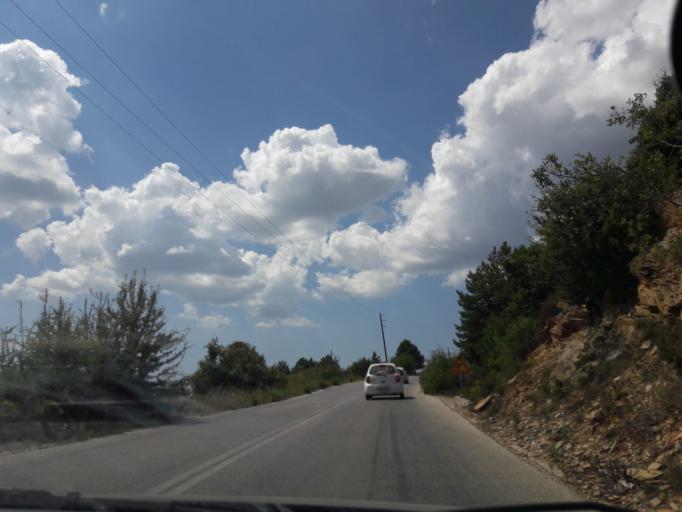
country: GR
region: Central Macedonia
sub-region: Nomos Chalkidikis
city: Polygyros
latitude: 40.3539
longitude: 23.4899
